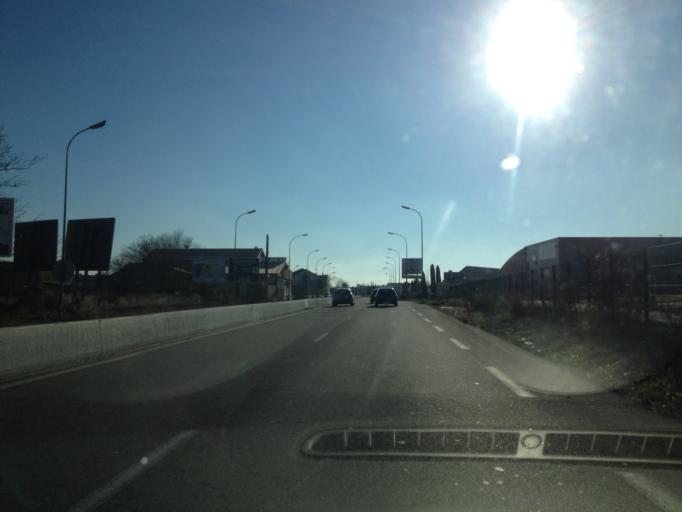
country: FR
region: Provence-Alpes-Cote d'Azur
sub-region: Departement du Vaucluse
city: Le Pontet
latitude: 43.9856
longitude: 4.8610
